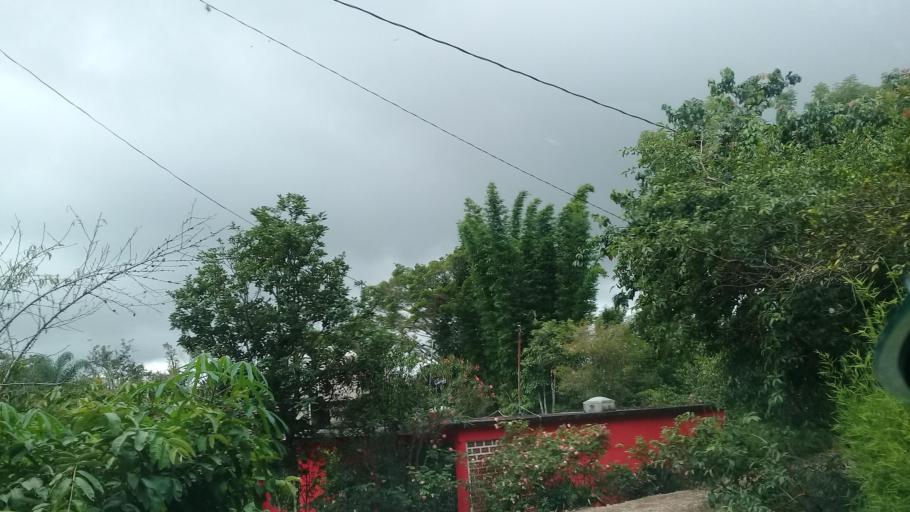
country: MX
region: Veracruz
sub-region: Xalapa
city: Colonia Santa Barbara
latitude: 19.4977
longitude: -96.8726
